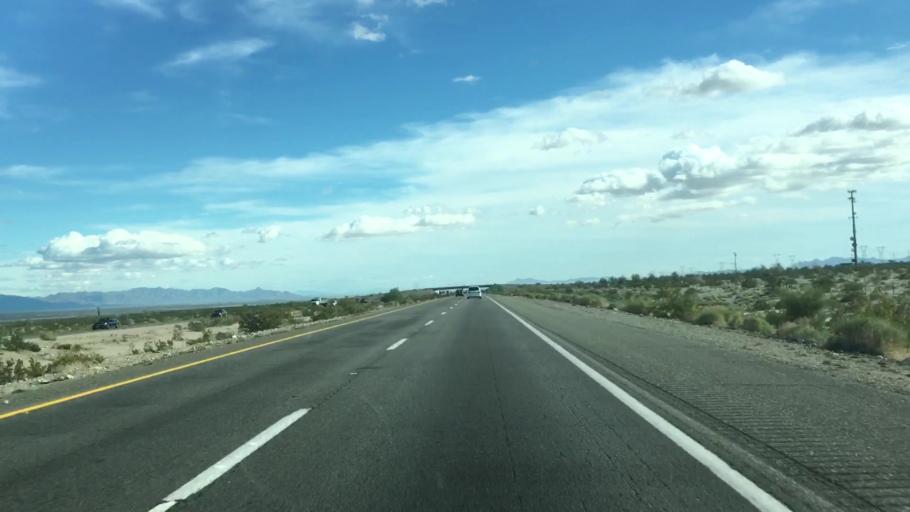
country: US
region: California
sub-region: Imperial County
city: Niland
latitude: 33.6850
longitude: -115.2525
